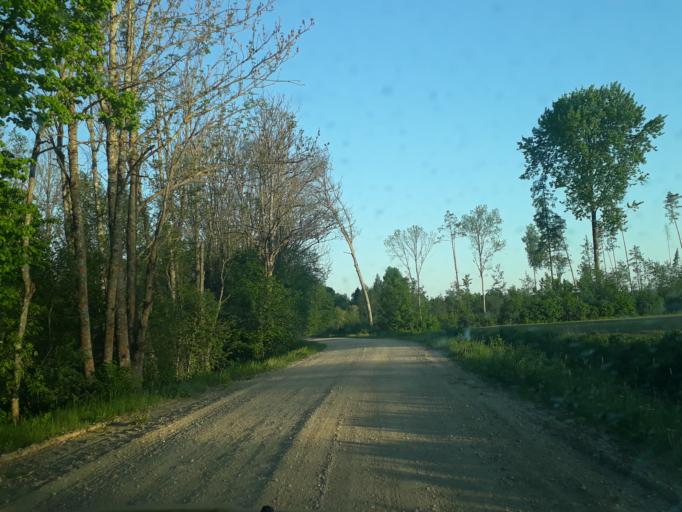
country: EE
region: Paernumaa
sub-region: Vaendra vald (alev)
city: Vandra
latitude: 58.5780
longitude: 24.9459
